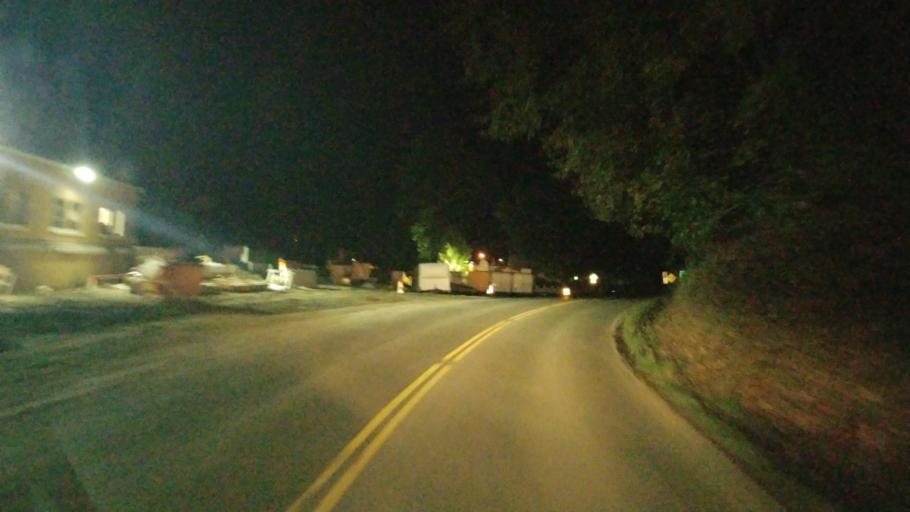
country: US
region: Ohio
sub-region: Hocking County
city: Logan
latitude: 39.5341
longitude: -82.4116
